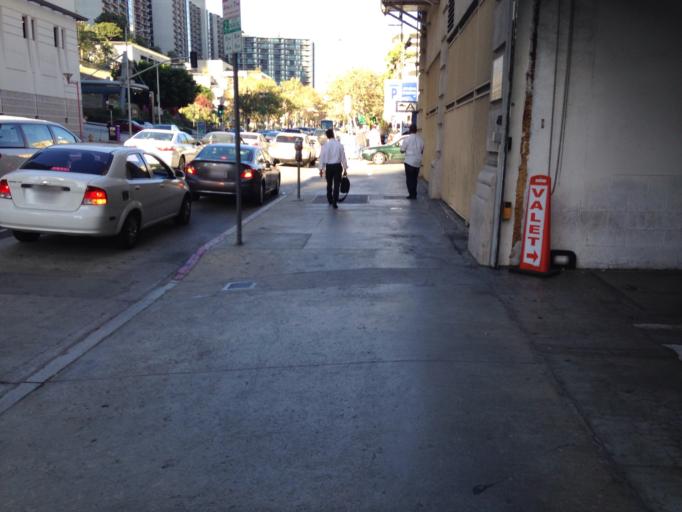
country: US
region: California
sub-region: Los Angeles County
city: Los Angeles
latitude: 34.0500
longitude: -118.2512
